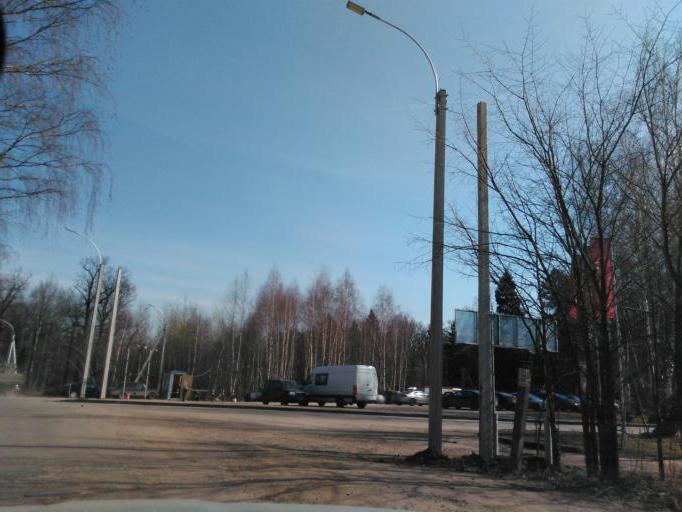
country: RU
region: Moskovskaya
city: Opalikha
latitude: 55.8869
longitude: 37.2651
